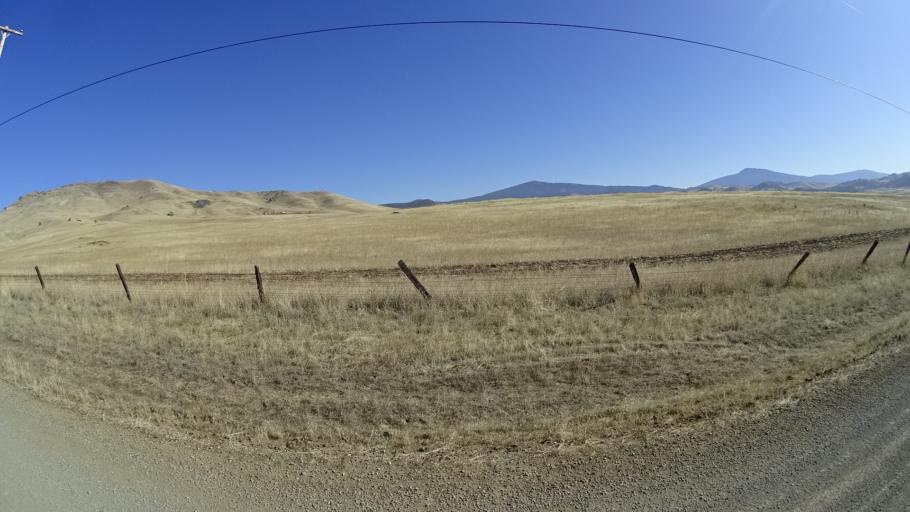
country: US
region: California
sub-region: Siskiyou County
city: Montague
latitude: 41.8406
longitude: -122.4206
